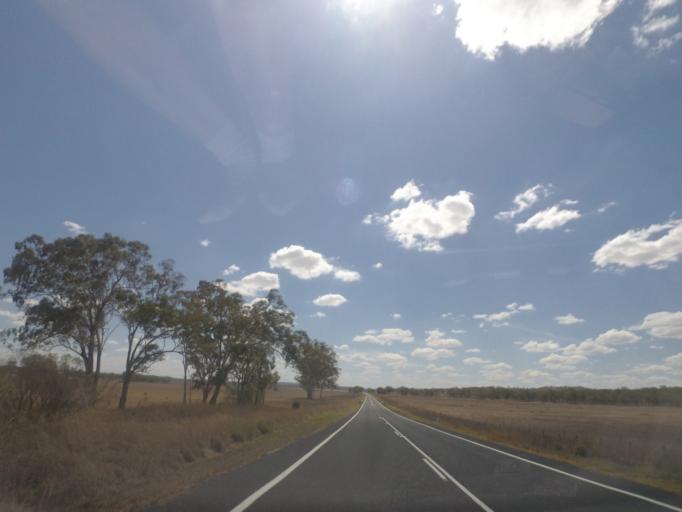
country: AU
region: Queensland
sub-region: Southern Downs
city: Warwick
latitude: -28.1827
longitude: 151.8039
